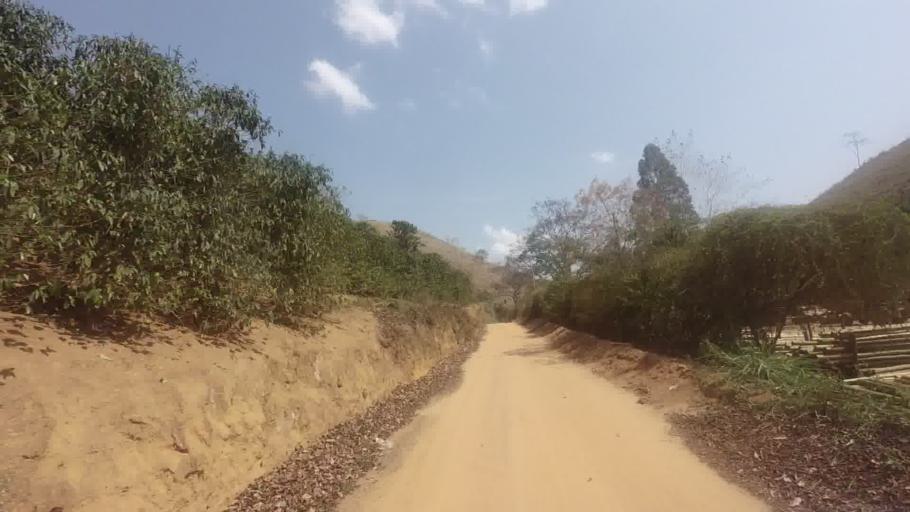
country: BR
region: Espirito Santo
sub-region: Mimoso Do Sul
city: Mimoso do Sul
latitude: -20.9905
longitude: -41.4999
